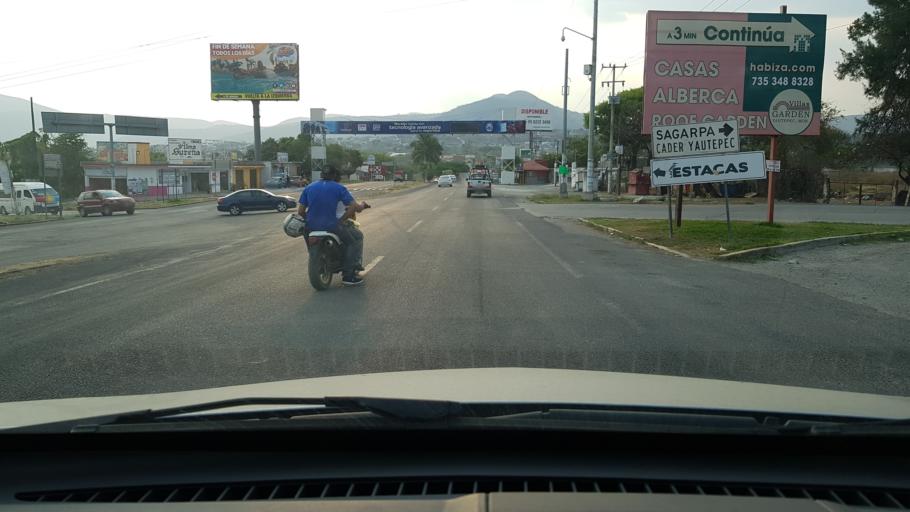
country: MX
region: Morelos
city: Yautepec
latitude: 18.8704
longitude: -99.0671
